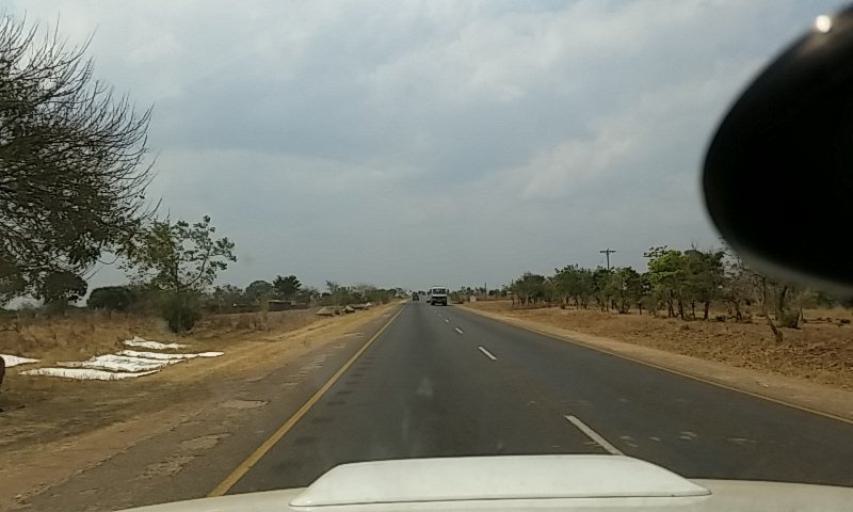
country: MW
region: Central Region
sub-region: Lilongwe District
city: Lilongwe
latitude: -13.8315
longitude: 33.8538
